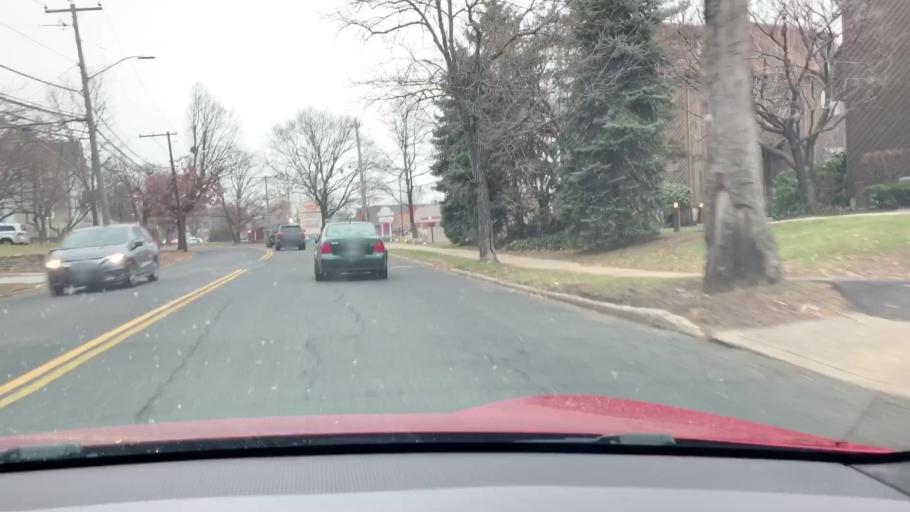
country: US
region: Connecticut
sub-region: Fairfield County
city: Stamford
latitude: 41.0752
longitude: -73.5230
